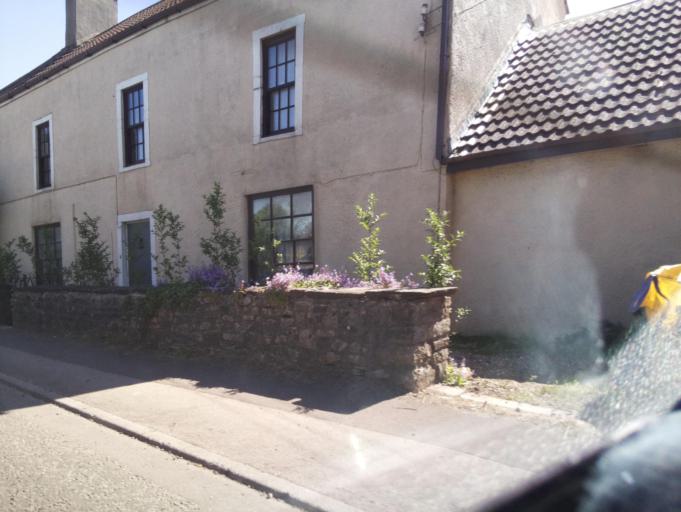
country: GB
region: England
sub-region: Bath and North East Somerset
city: Clutton
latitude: 51.3288
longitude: -2.5478
